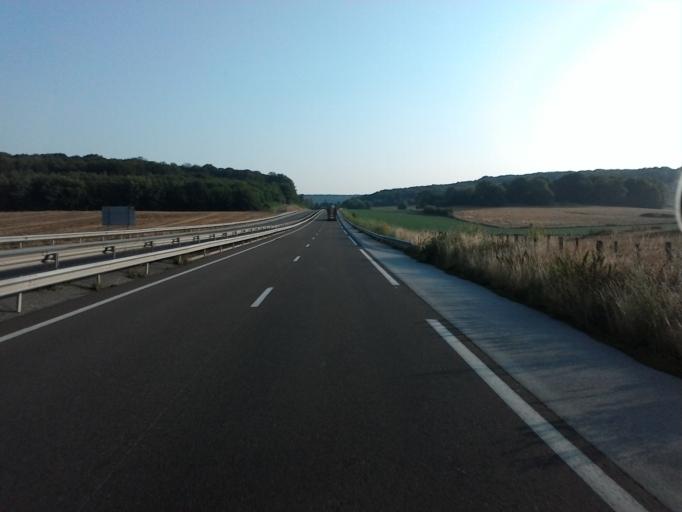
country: FR
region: Franche-Comte
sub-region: Departement de la Haute-Saone
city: Echenoz-la-Meline
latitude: 47.5620
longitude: 6.1380
